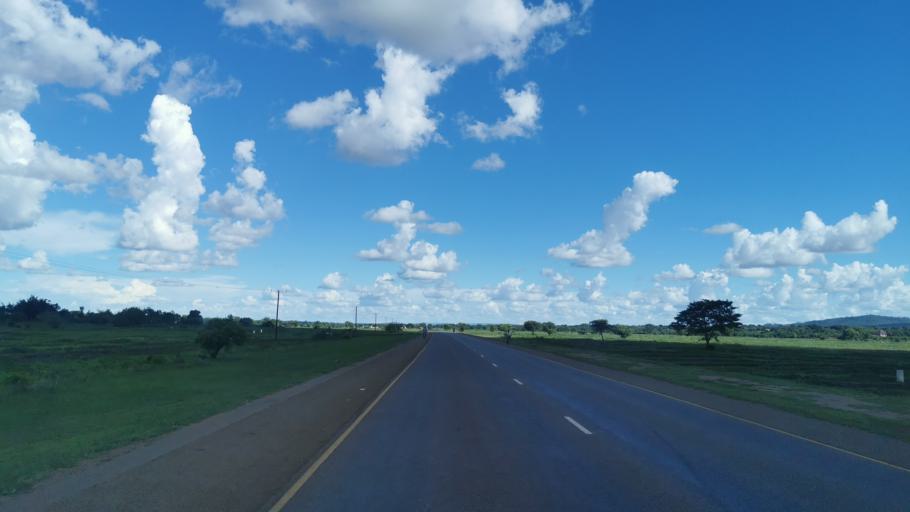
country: TZ
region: Geita
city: Ushirombo
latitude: -3.4780
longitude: 31.9171
